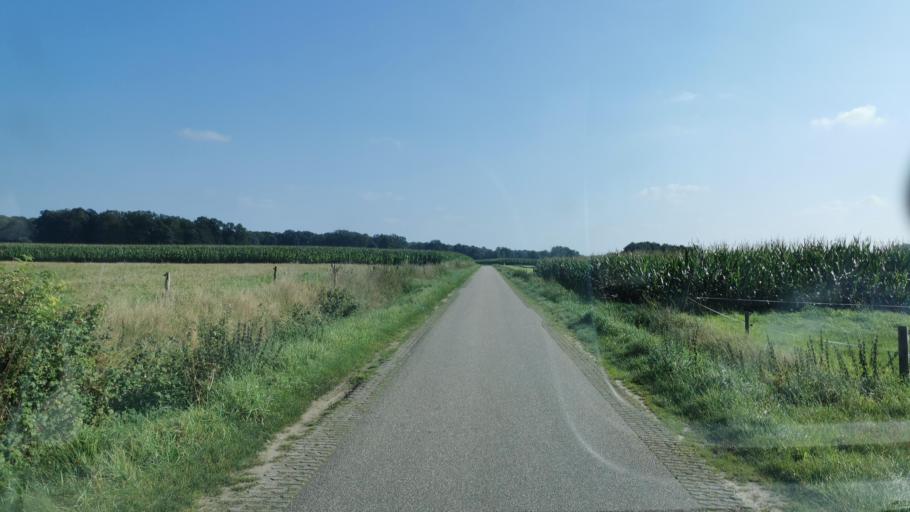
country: DE
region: Lower Saxony
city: Lage
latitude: 52.4021
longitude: 6.9474
